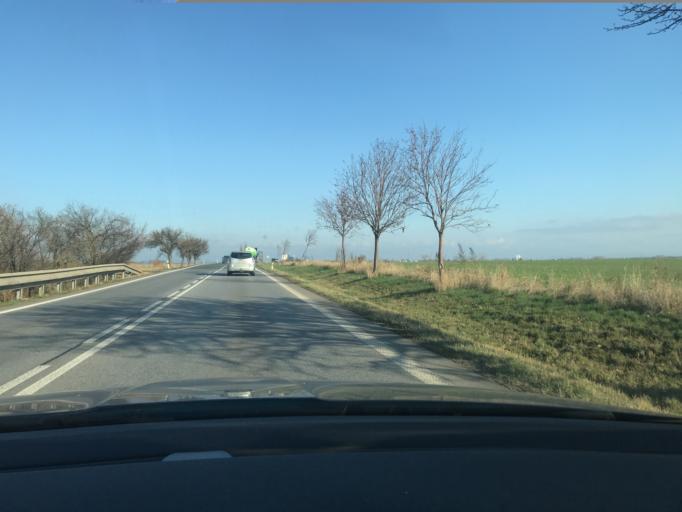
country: CZ
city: Predmerice nad Labem
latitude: 50.2824
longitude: 15.8198
